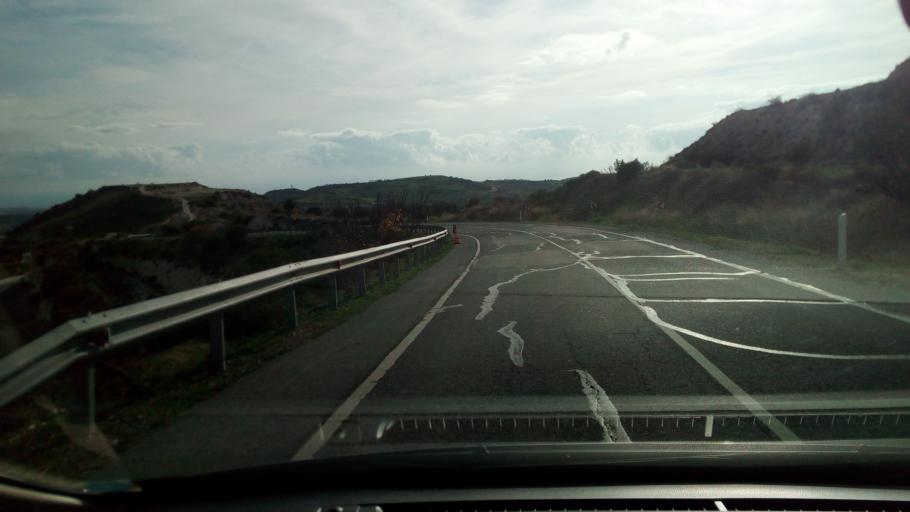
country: CY
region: Pafos
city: Mesogi
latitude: 34.7951
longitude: 32.5472
